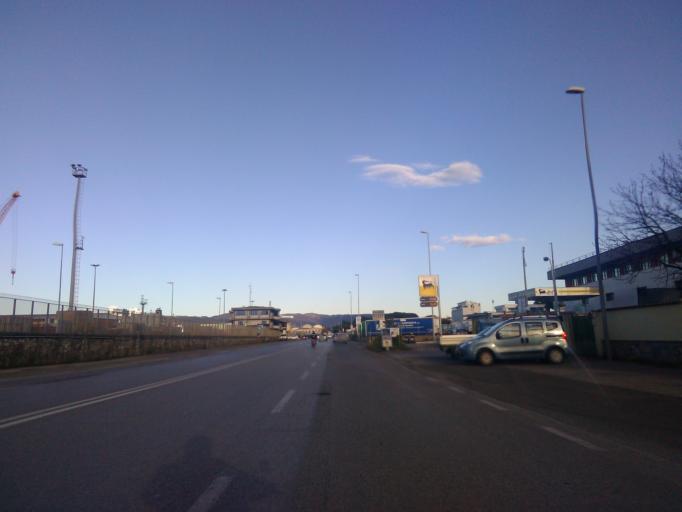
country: IT
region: Tuscany
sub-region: Provincia di Massa-Carrara
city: Marina di Carrara
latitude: 44.0341
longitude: 10.0493
